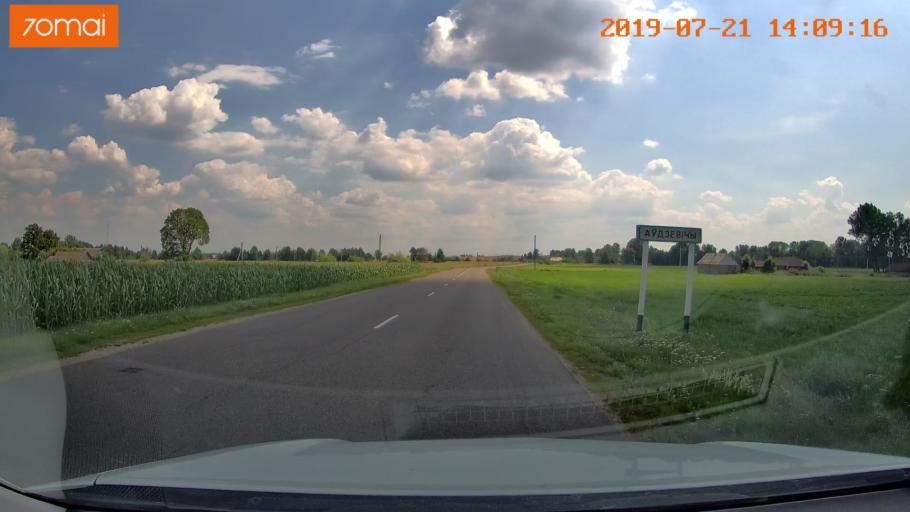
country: BY
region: Grodnenskaya
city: Karelichy
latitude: 53.6684
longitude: 26.1313
